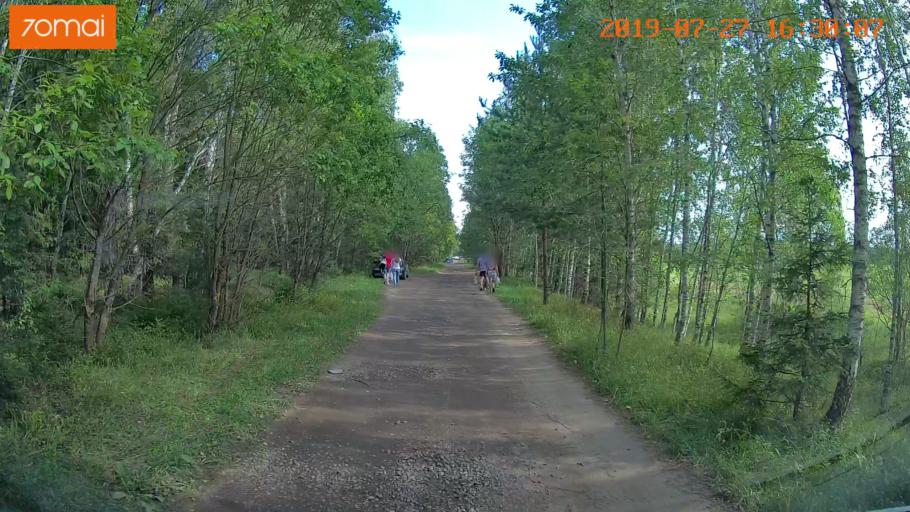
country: RU
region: Ivanovo
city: Novo-Talitsy
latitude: 57.0928
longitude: 40.8517
